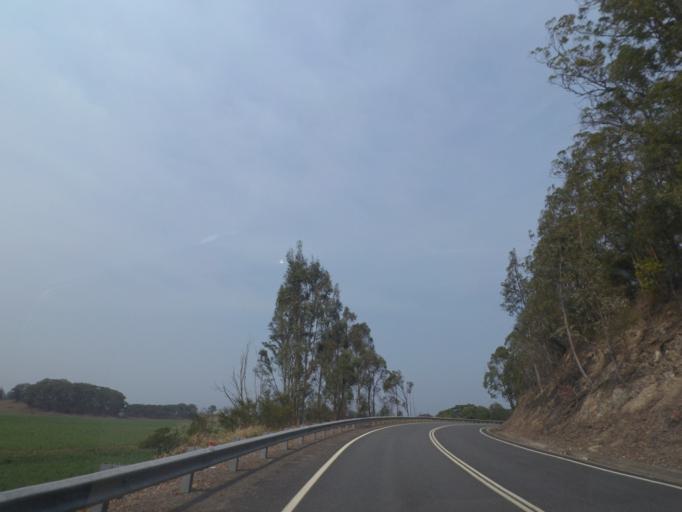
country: AU
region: New South Wales
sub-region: Tweed
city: Burringbar
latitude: -28.4581
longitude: 153.5211
